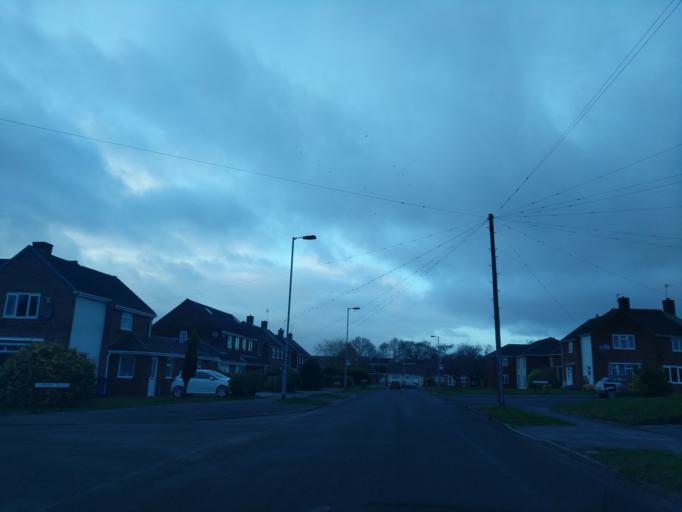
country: GB
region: England
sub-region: Staffordshire
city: Cannock
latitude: 52.6852
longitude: -2.0480
